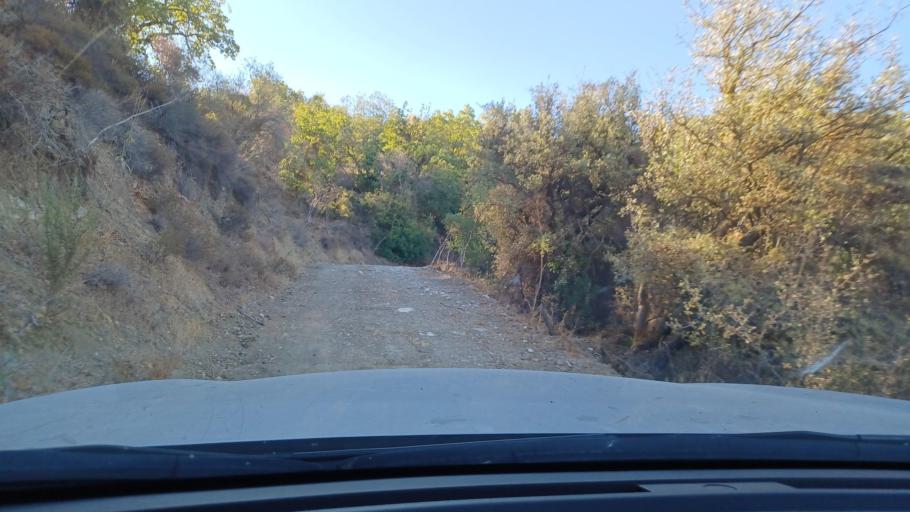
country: CY
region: Pafos
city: Polis
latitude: 34.9968
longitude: 32.5059
